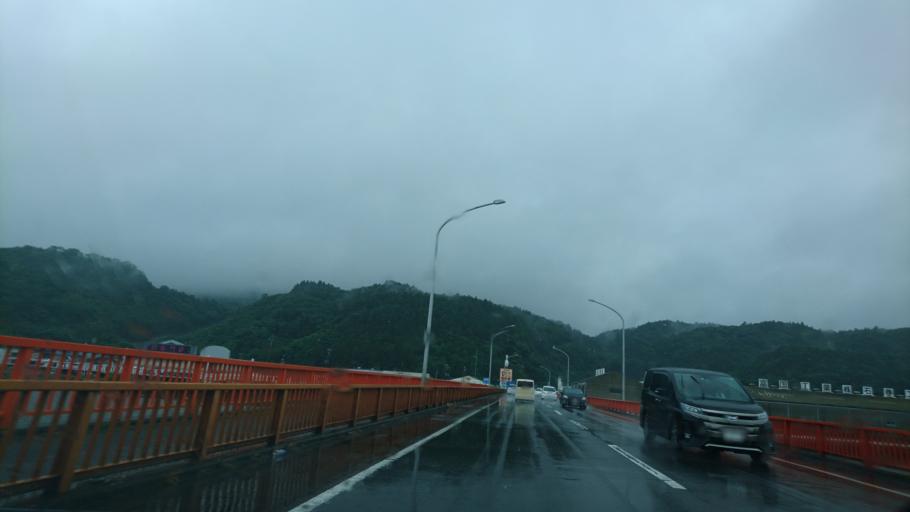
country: JP
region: Miyagi
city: Ishinomaki
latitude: 38.4381
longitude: 141.3166
